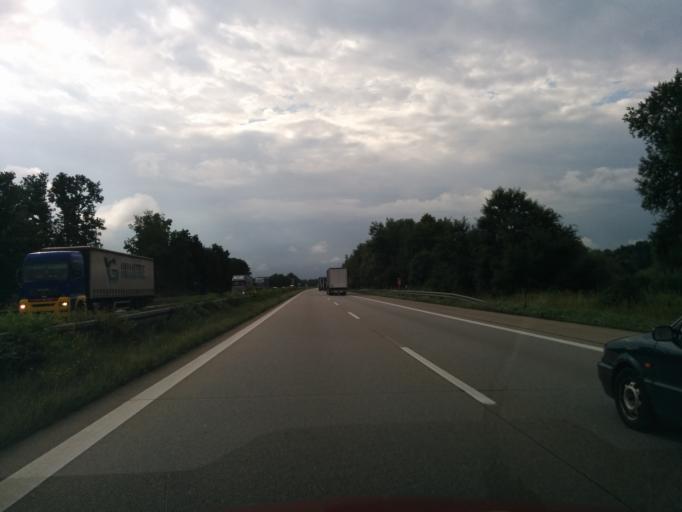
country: DE
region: Bavaria
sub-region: Lower Bavaria
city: Deggendorf
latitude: 48.8001
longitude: 12.9869
